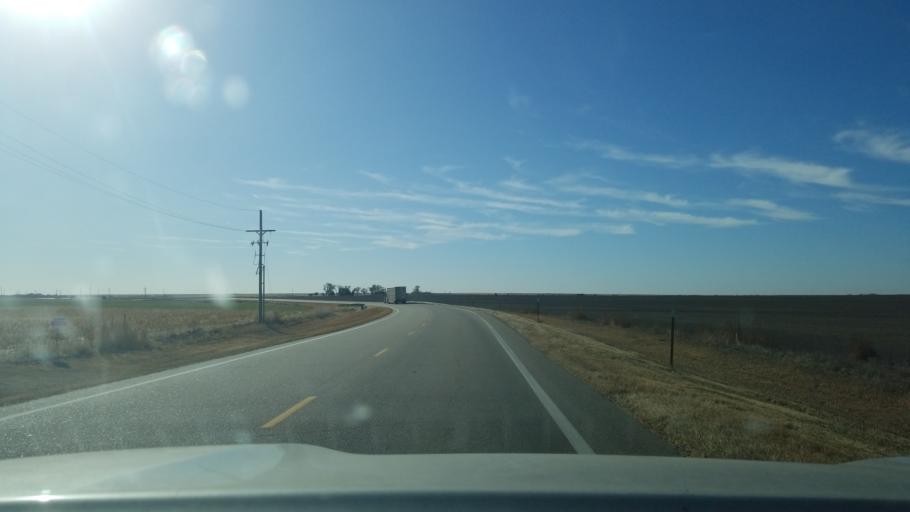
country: US
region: Kansas
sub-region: Ness County
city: Ness City
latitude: 38.4349
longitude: -99.9047
